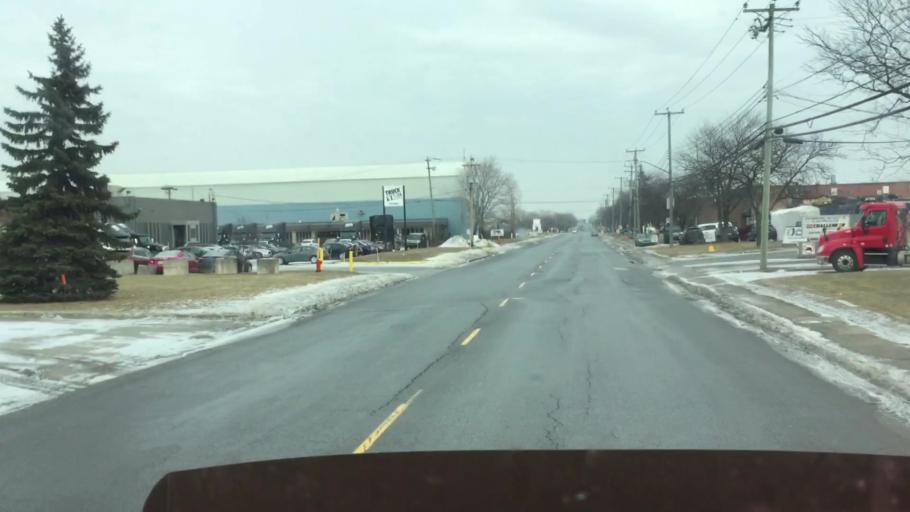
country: CA
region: Quebec
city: Dollard-Des Ormeaux
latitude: 45.4786
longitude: -73.7850
